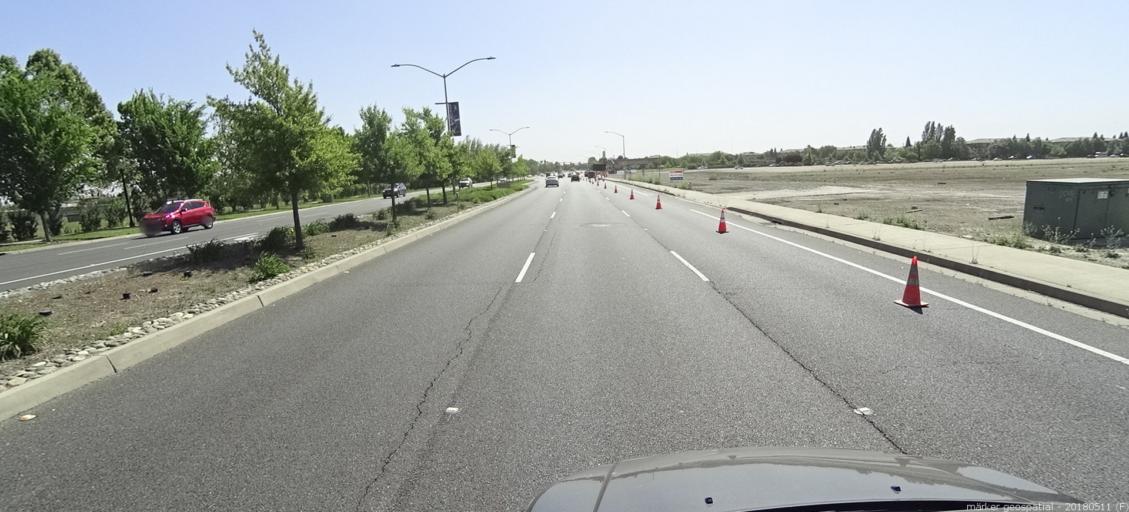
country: US
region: California
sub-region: Sacramento County
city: Rio Linda
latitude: 38.6559
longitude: -121.5154
